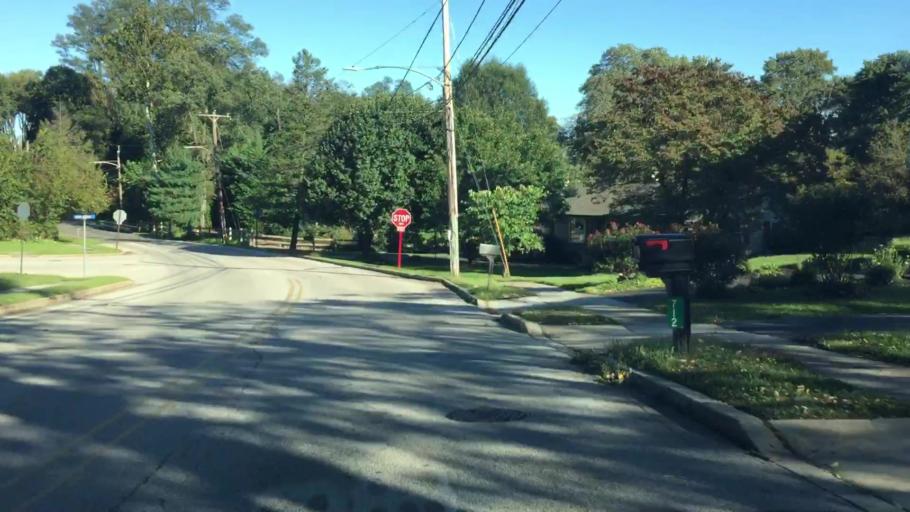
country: US
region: Pennsylvania
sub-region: Delaware County
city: Village Green-Green Ridge
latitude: 39.8694
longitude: -75.4459
